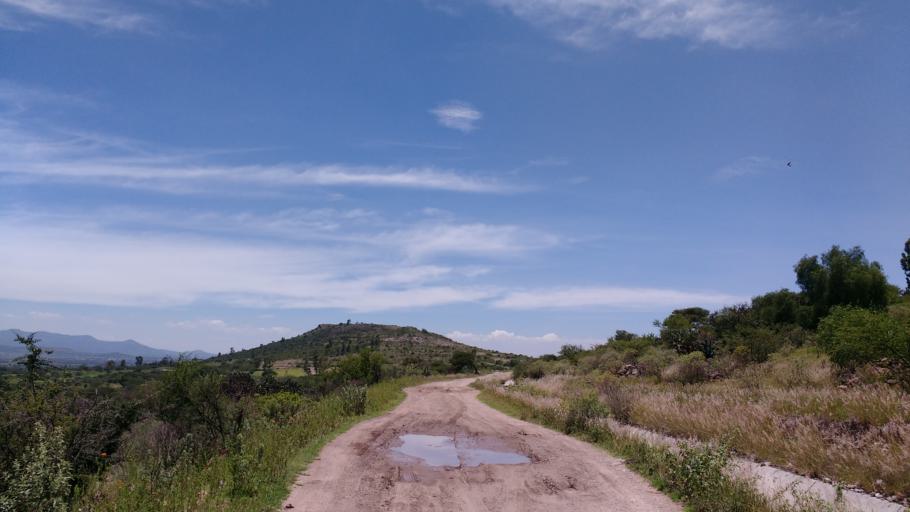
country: MX
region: Hidalgo
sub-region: Tezontepec de Aldama
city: Tenango
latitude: 20.2347
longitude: -99.2737
